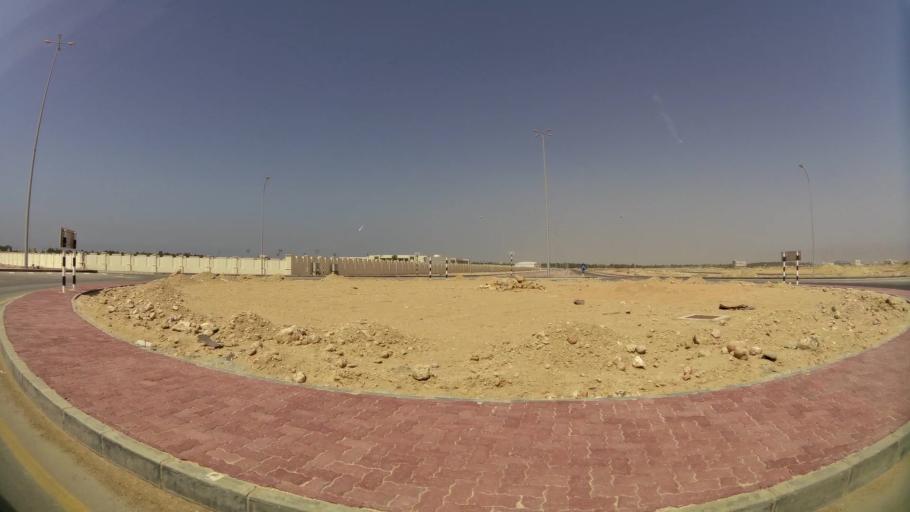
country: OM
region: Zufar
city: Salalah
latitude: 17.0344
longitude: 54.1341
